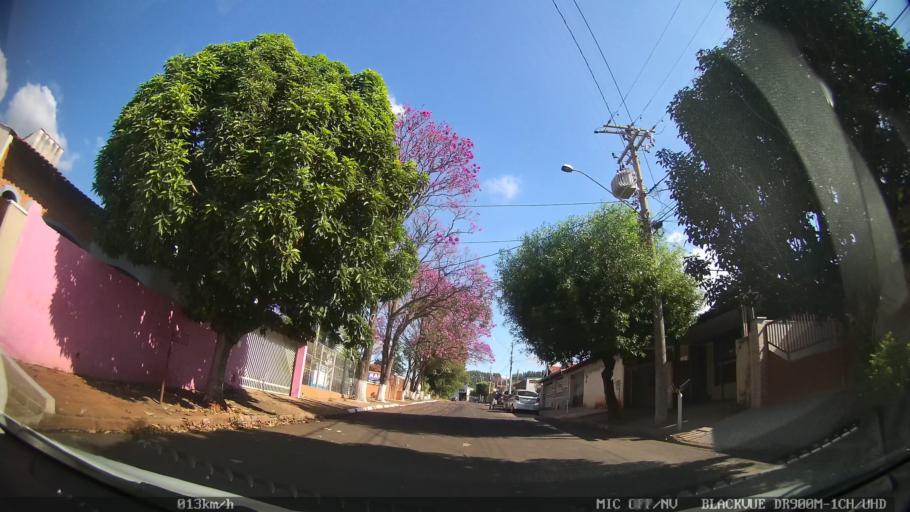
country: BR
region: Sao Paulo
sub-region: Sumare
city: Sumare
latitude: -22.8348
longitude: -47.2615
